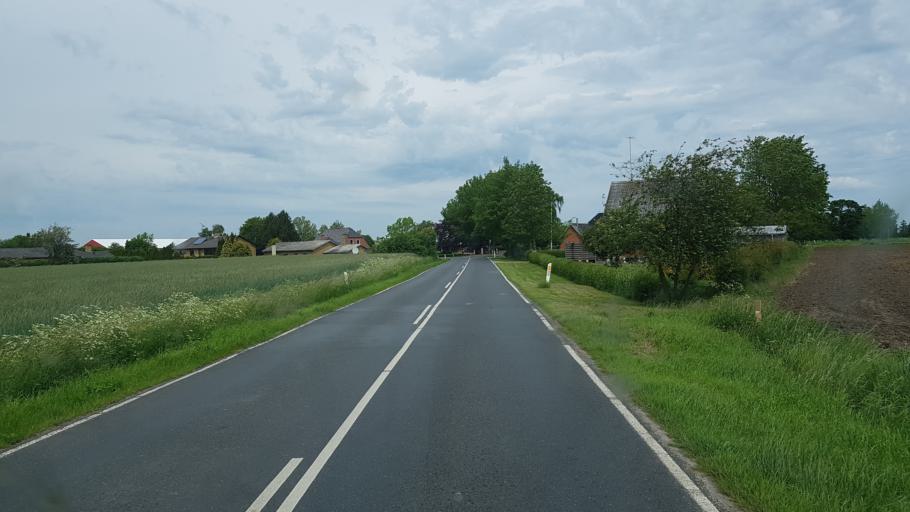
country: DK
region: South Denmark
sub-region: Nordfyns Kommune
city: Sonderso
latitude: 55.5688
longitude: 10.2135
